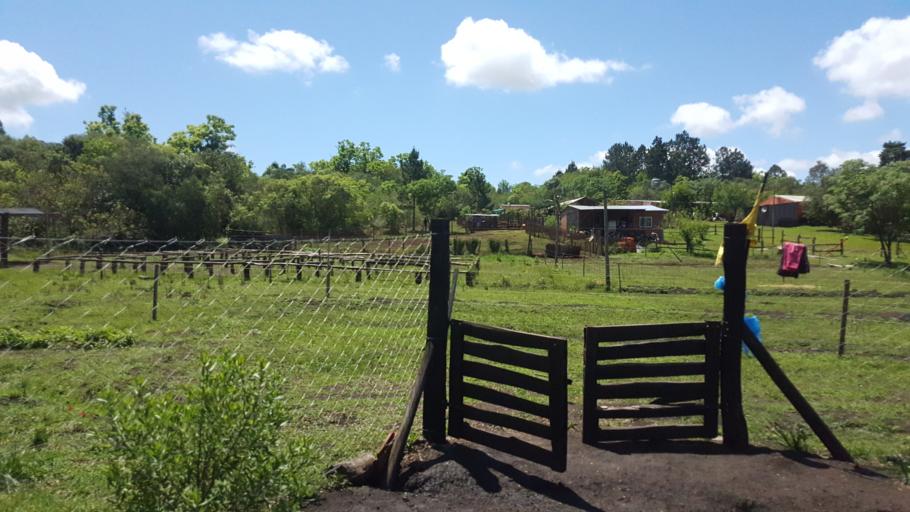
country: AR
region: Misiones
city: Garupa
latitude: -27.5037
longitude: -55.8547
